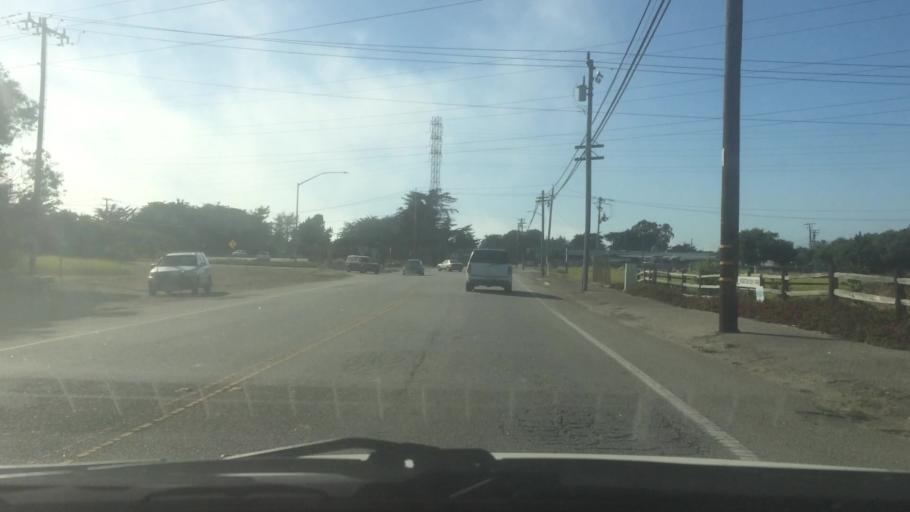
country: US
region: California
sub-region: San Luis Obispo County
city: Morro Bay
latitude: 35.3749
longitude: -120.8519
